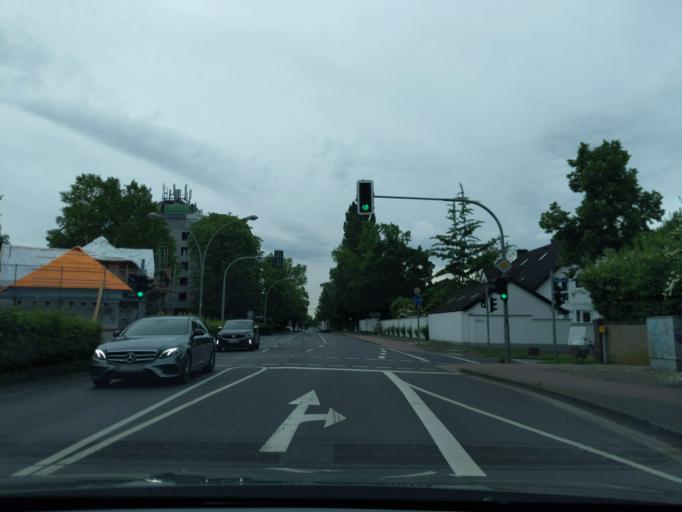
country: DE
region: North Rhine-Westphalia
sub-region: Regierungsbezirk Dusseldorf
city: Meerbusch
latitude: 51.2622
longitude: 6.6766
